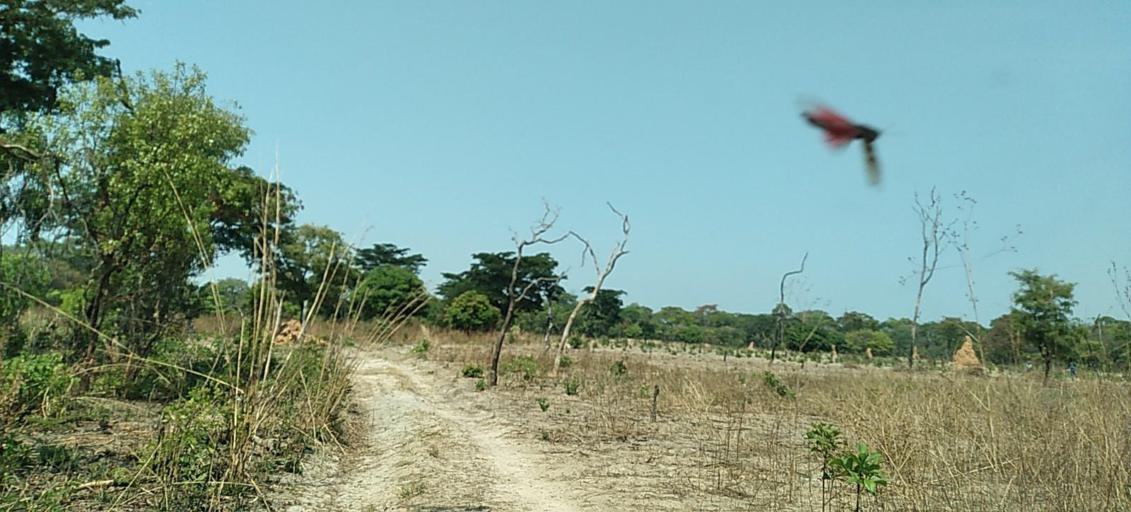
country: ZM
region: Copperbelt
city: Mpongwe
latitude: -13.7924
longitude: 28.0903
